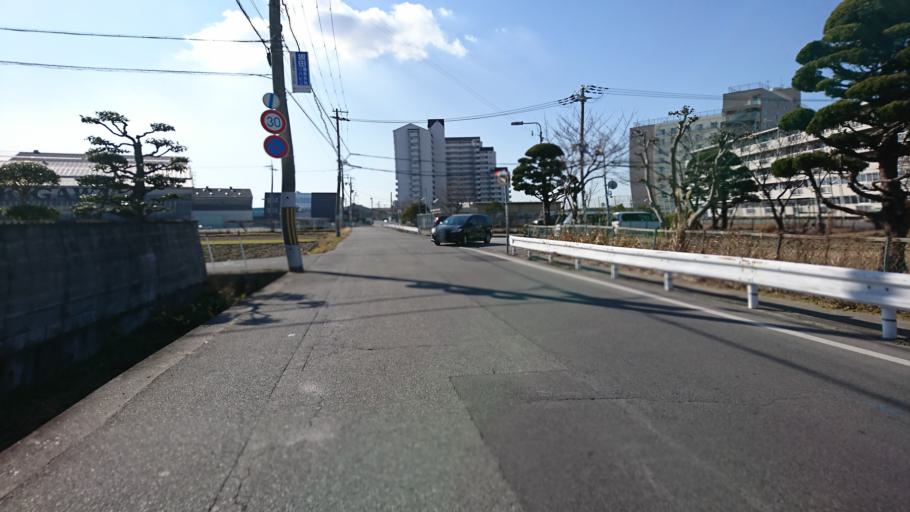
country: JP
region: Hyogo
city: Kakogawacho-honmachi
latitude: 34.7332
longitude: 134.8670
